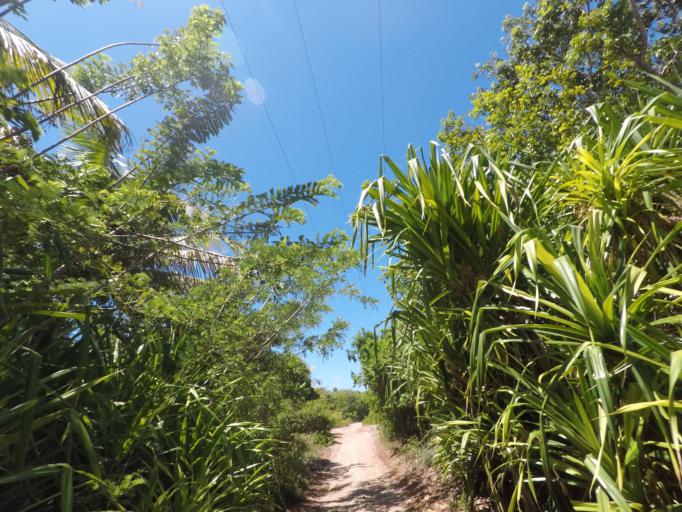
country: BR
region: Bahia
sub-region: Marau
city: Marau
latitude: -14.0096
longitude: -38.9446
